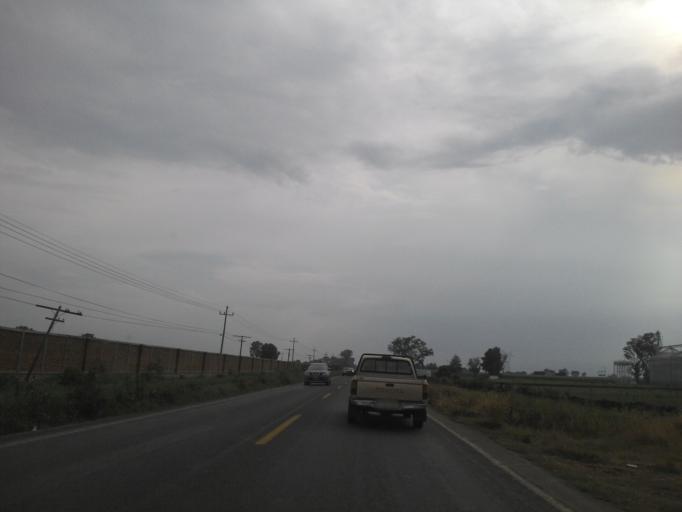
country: MX
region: Jalisco
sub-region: Acatic
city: Tierras Coloradas
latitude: 20.7524
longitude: -102.8321
